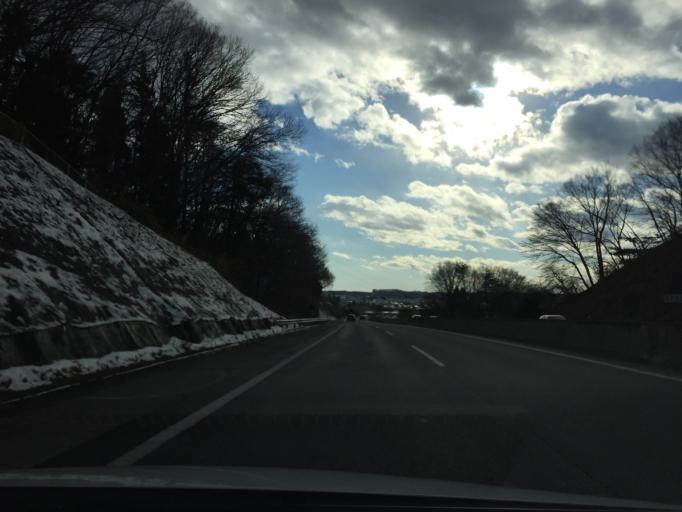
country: JP
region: Fukushima
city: Sukagawa
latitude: 37.1448
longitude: 140.2007
